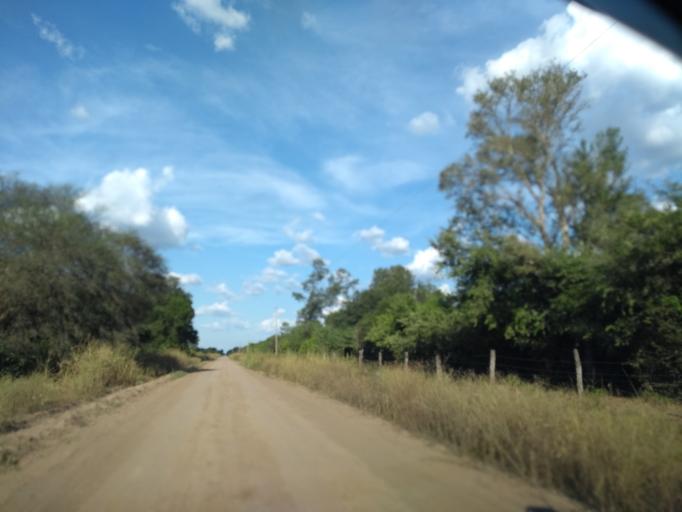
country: AR
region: Chaco
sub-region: Departamento de Quitilipi
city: Quitilipi
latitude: -26.7489
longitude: -60.2660
